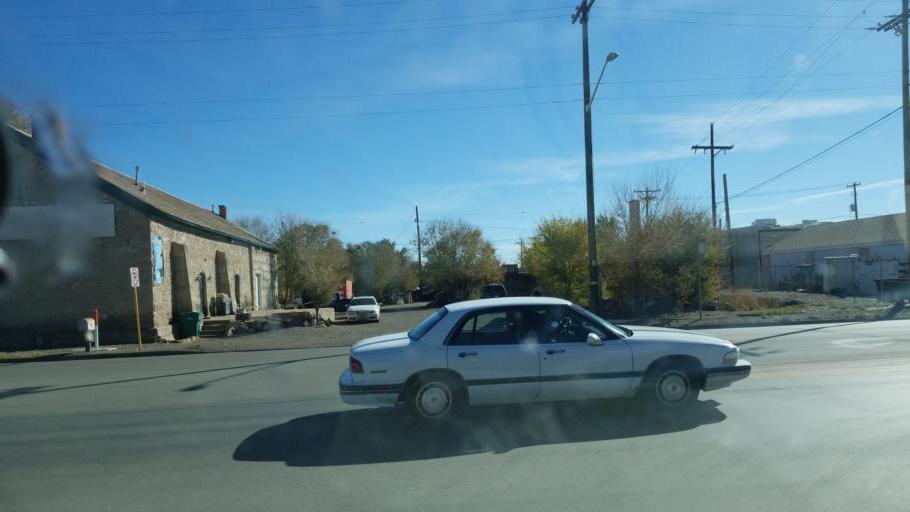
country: US
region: Colorado
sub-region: Rio Grande County
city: Monte Vista
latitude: 37.5817
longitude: -106.1496
